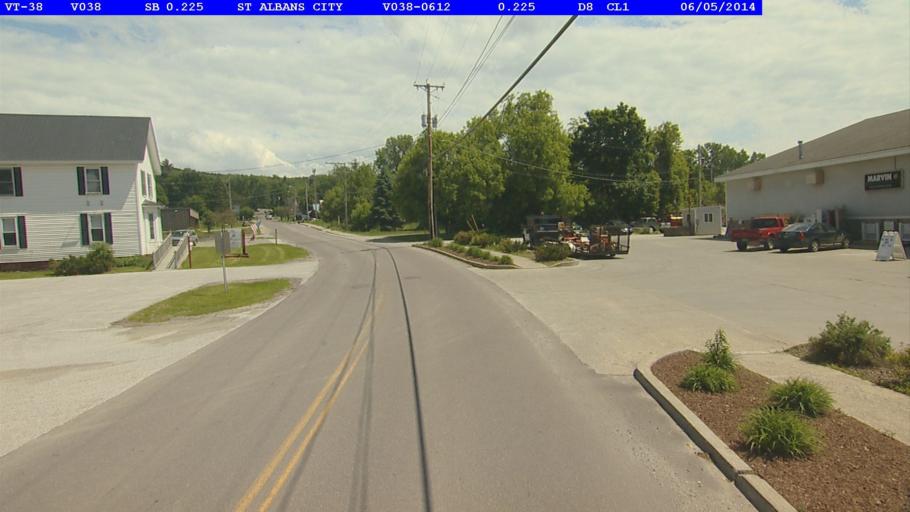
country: US
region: Vermont
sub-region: Franklin County
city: Saint Albans
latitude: 44.8203
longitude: -73.0861
